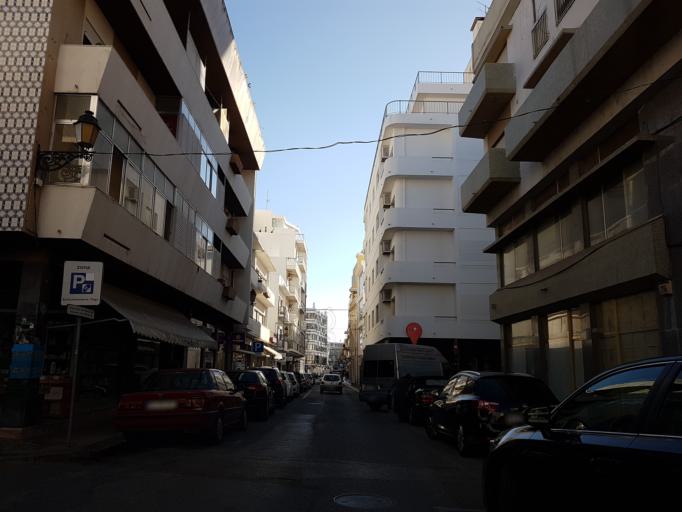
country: PT
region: Faro
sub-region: Faro
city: Faro
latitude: 37.0173
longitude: -7.9317
